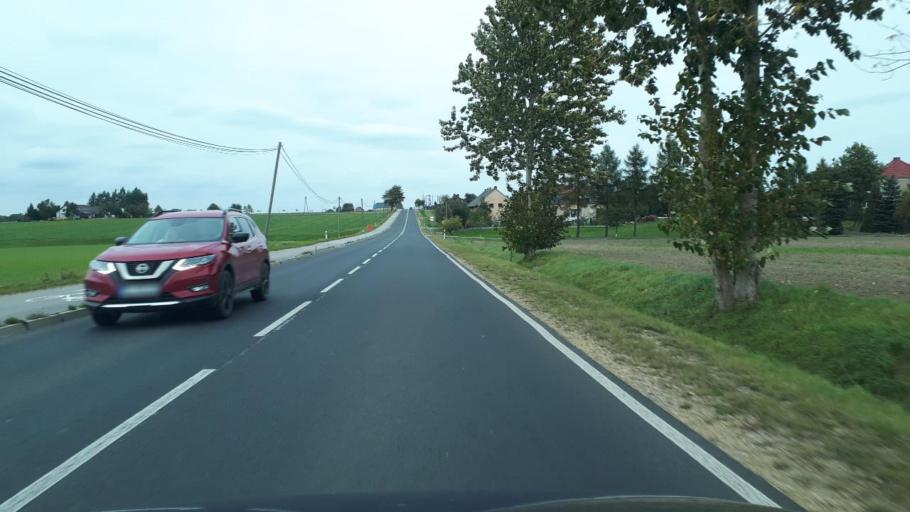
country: PL
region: Opole Voivodeship
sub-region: Powiat oleski
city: Olesno
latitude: 50.8491
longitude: 18.4139
